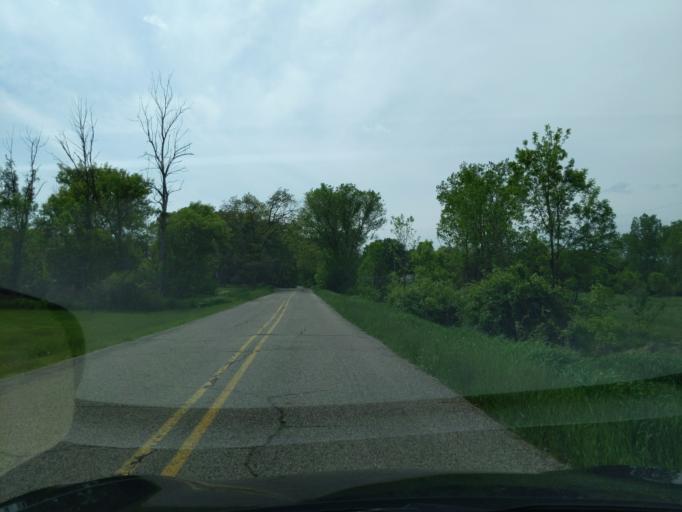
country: US
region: Michigan
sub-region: Ingham County
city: Leslie
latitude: 42.4319
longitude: -84.3480
